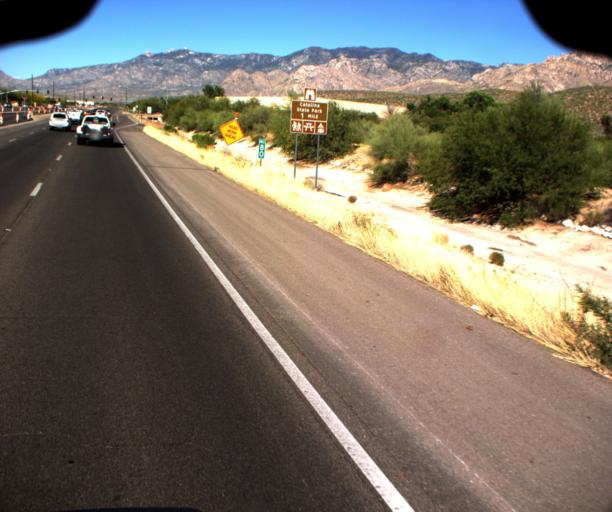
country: US
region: Arizona
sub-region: Pima County
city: Oro Valley
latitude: 32.4049
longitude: -110.9489
